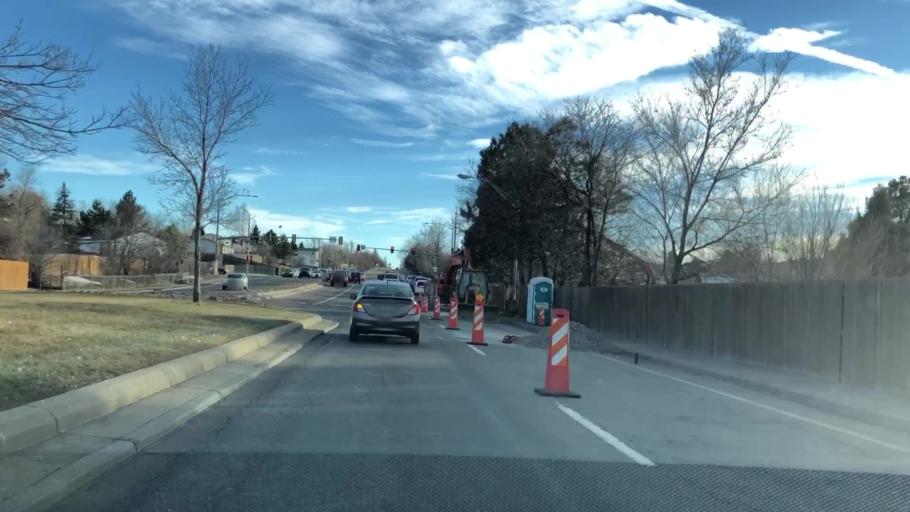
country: US
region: Colorado
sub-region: Adams County
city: Aurora
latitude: 39.6545
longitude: -104.7914
